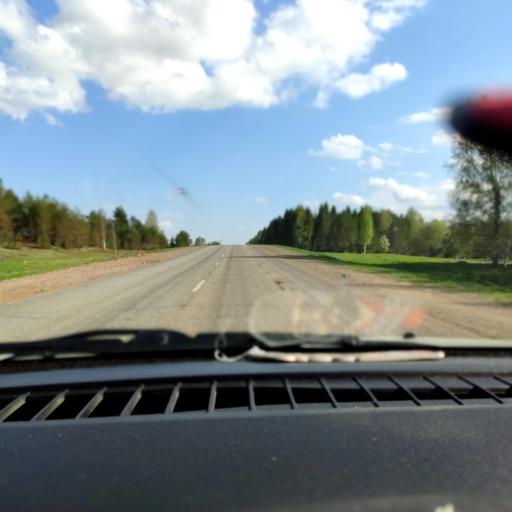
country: RU
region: Perm
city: Karagay
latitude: 58.4751
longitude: 54.7862
